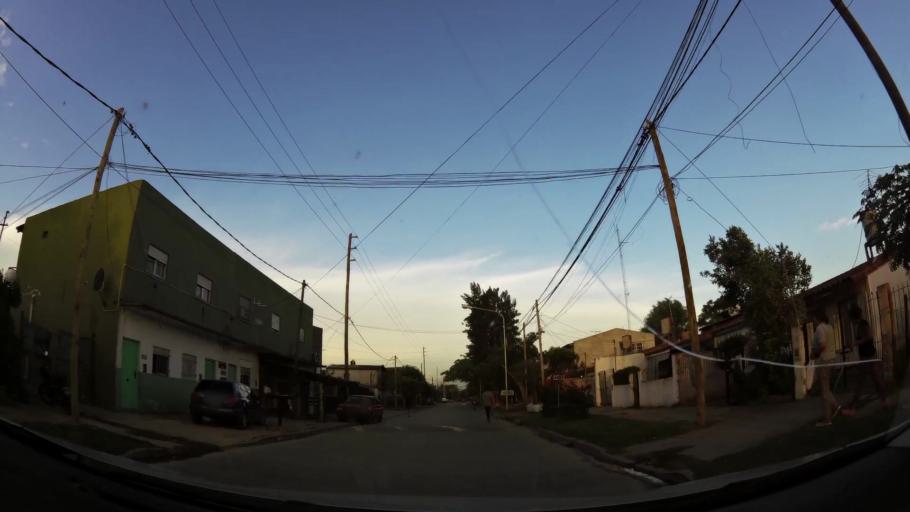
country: AR
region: Buenos Aires
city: Santa Catalina - Dique Lujan
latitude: -34.4357
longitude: -58.6702
